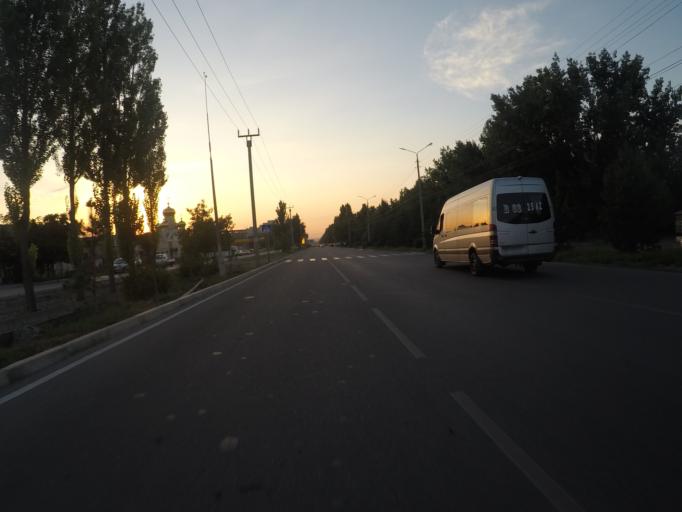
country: KG
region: Chuy
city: Bishkek
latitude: 42.8118
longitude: 74.6334
